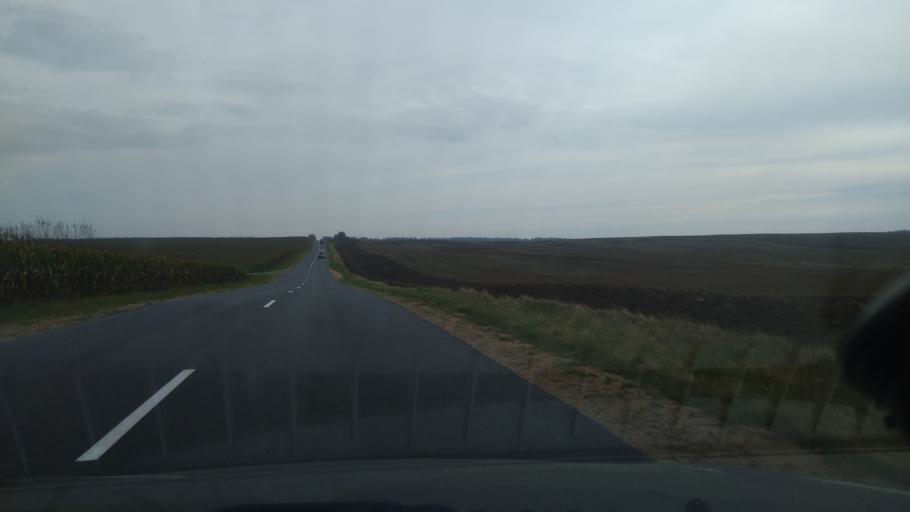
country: BY
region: Minsk
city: Rudzyensk
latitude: 53.6153
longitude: 27.7474
